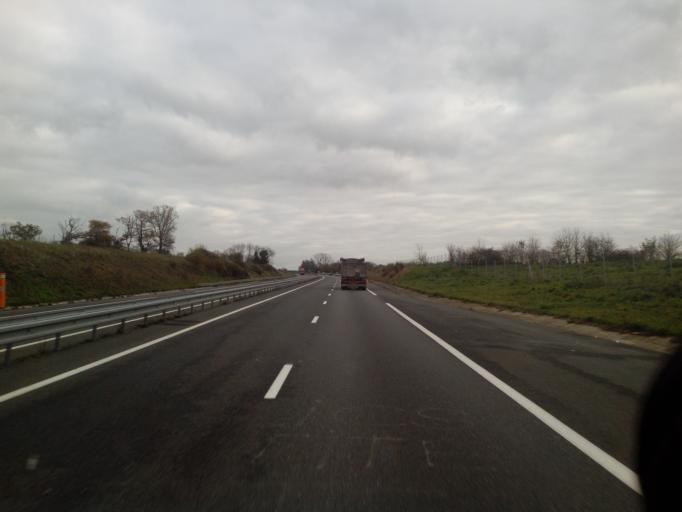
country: FR
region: Poitou-Charentes
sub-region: Departement des Deux-Sevres
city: Saint-Pierre-des-Echaubrognes
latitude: 46.9538
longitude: -0.7752
